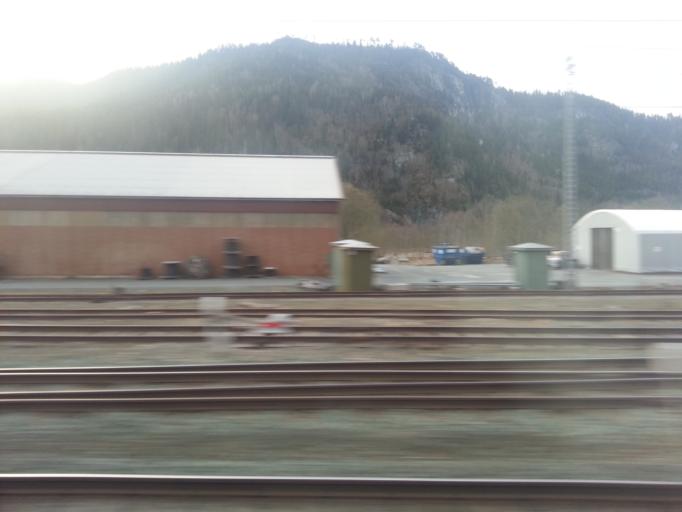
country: NO
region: Sor-Trondelag
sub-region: Midtre Gauldal
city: Storen
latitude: 63.0566
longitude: 10.2860
